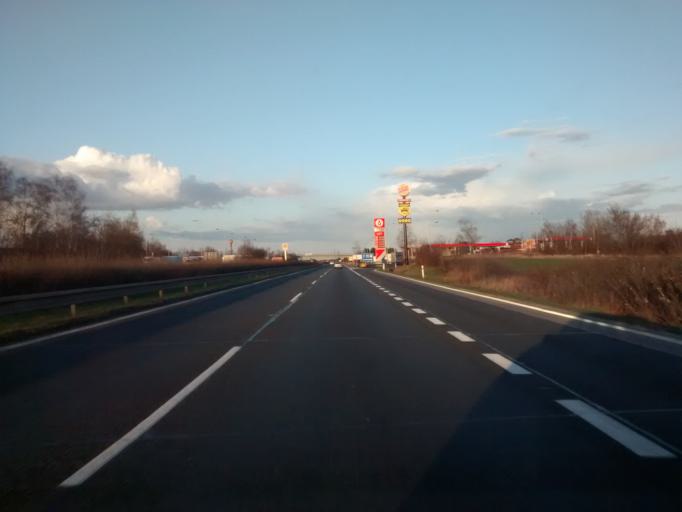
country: CZ
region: Praha
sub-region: Praha 20
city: Horni Pocernice
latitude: 50.1079
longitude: 14.6347
